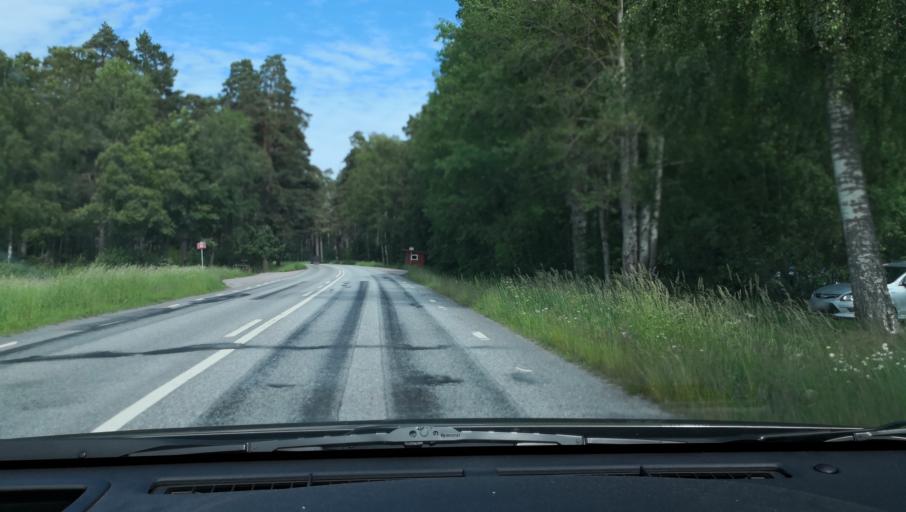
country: SE
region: Uppsala
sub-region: Uppsala Kommun
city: Saevja
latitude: 59.7699
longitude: 17.6522
